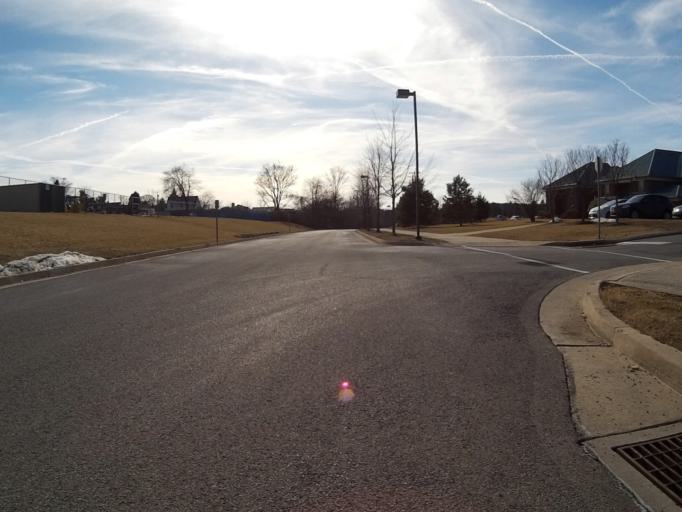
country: US
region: Pennsylvania
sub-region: Centre County
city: State College
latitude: 40.7885
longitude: -77.8724
